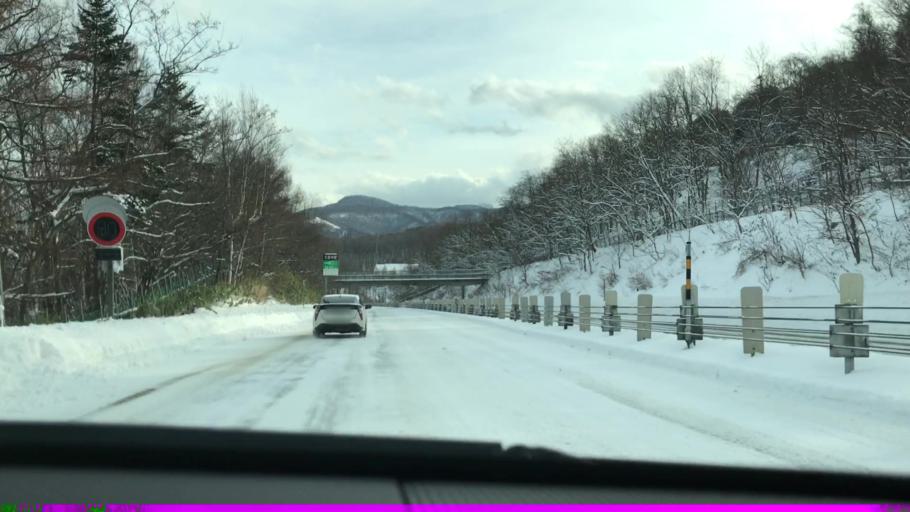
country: JP
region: Hokkaido
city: Otaru
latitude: 43.1500
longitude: 141.1290
